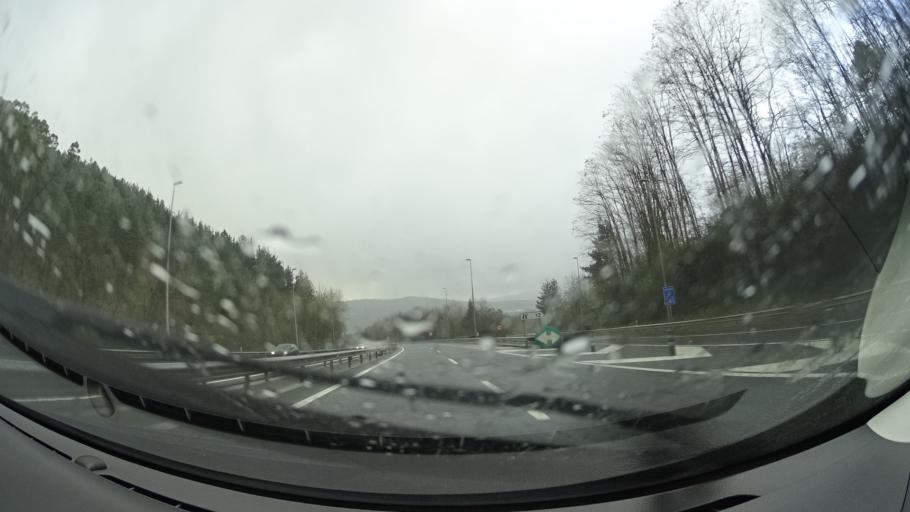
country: ES
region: Basque Country
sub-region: Bizkaia
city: Derio
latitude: 43.3106
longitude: -2.8798
